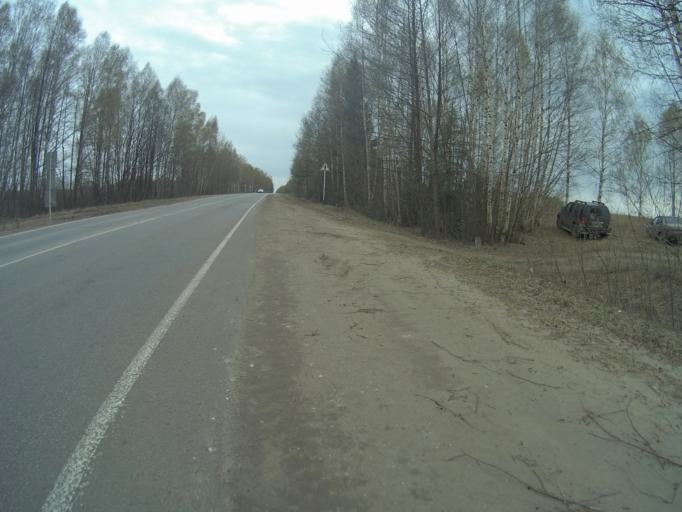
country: RU
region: Vladimir
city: Golovino
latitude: 55.9461
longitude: 40.5821
